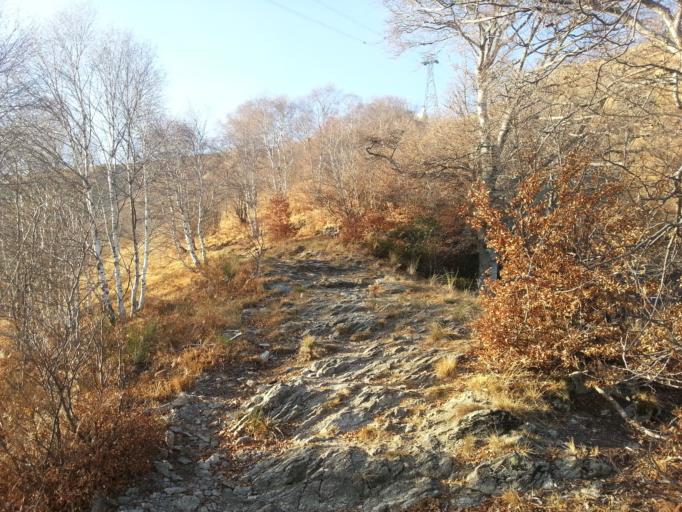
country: IT
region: Lombardy
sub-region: Provincia di Varese
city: Curiglia
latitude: 46.0363
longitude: 8.8414
